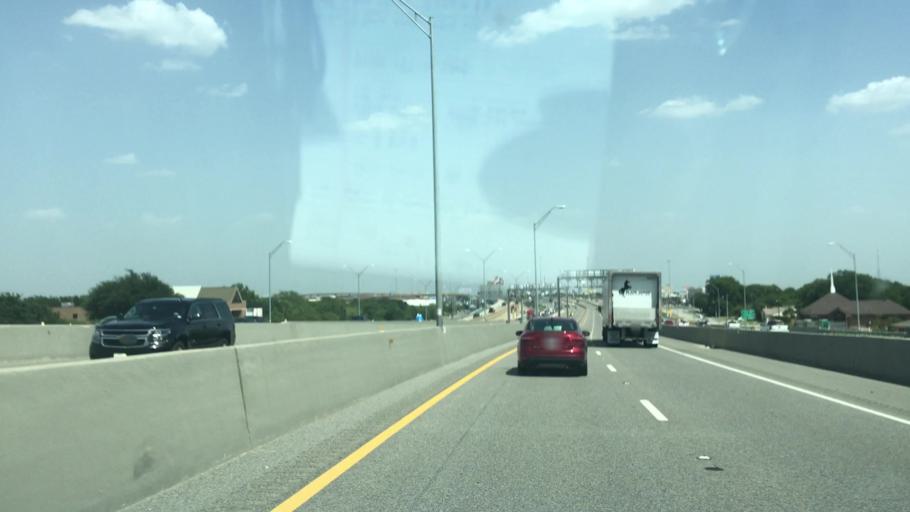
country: US
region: Texas
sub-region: Tarrant County
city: North Richland Hills
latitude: 32.8382
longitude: -97.2271
